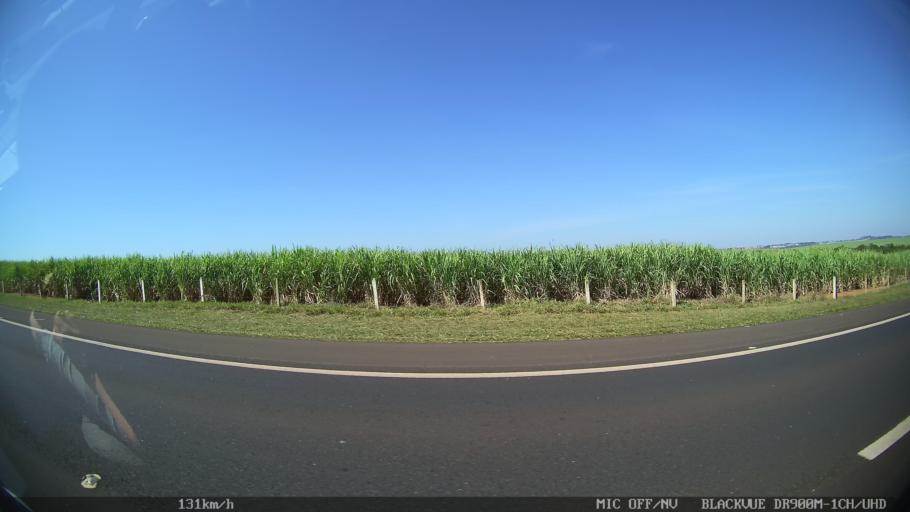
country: BR
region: Sao Paulo
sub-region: Batatais
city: Batatais
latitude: -20.8211
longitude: -47.5893
